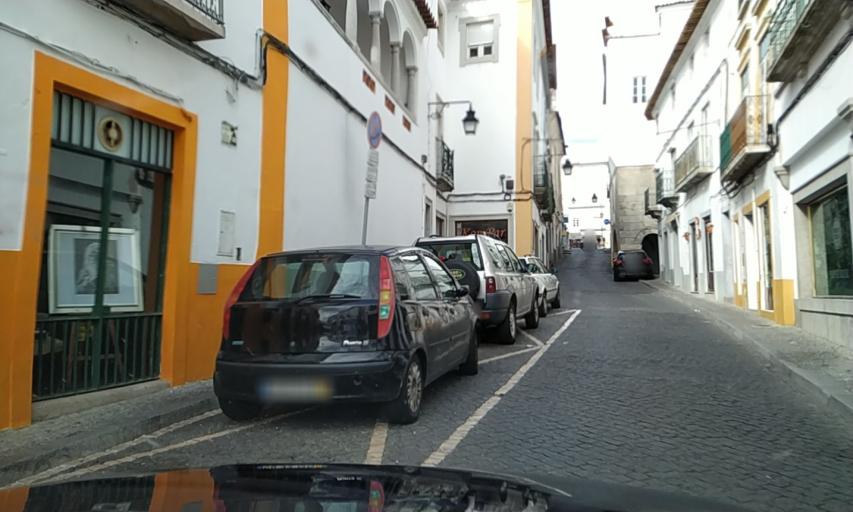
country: PT
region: Evora
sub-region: Evora
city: Evora
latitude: 38.5702
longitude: -7.9101
